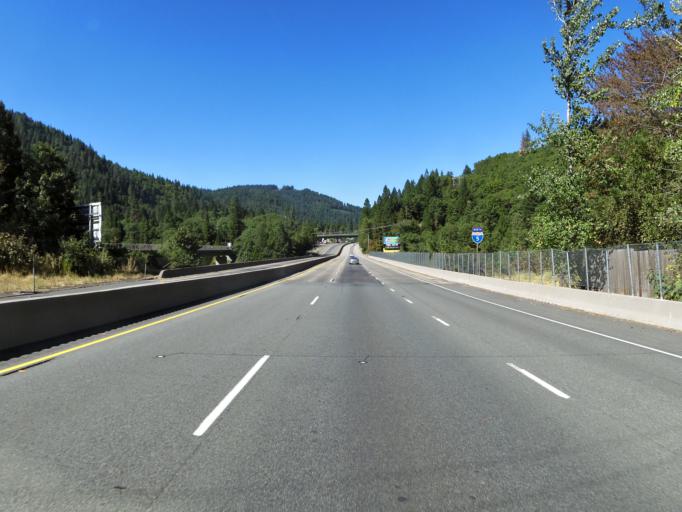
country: US
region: California
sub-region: Siskiyou County
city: Dunsmuir
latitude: 41.2192
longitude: -122.2748
